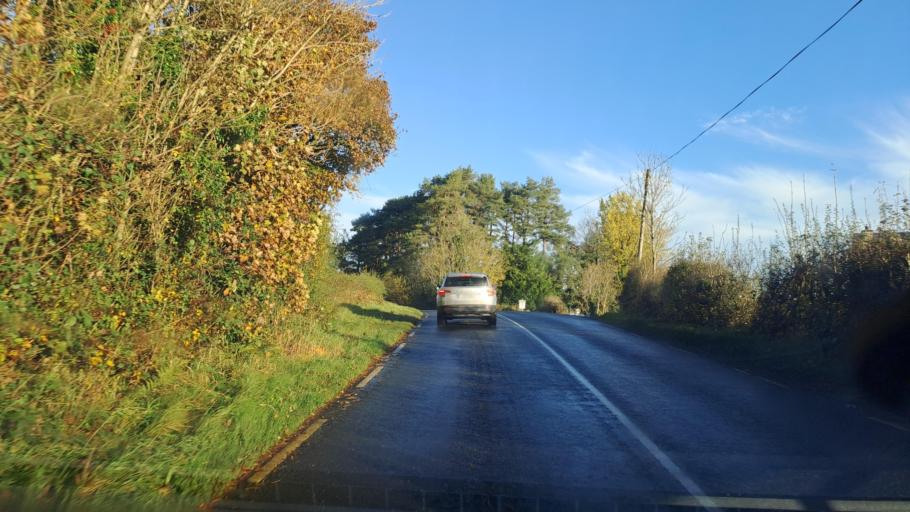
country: IE
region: Ulster
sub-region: An Cabhan
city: Cootehill
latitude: 54.1306
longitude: -7.0001
